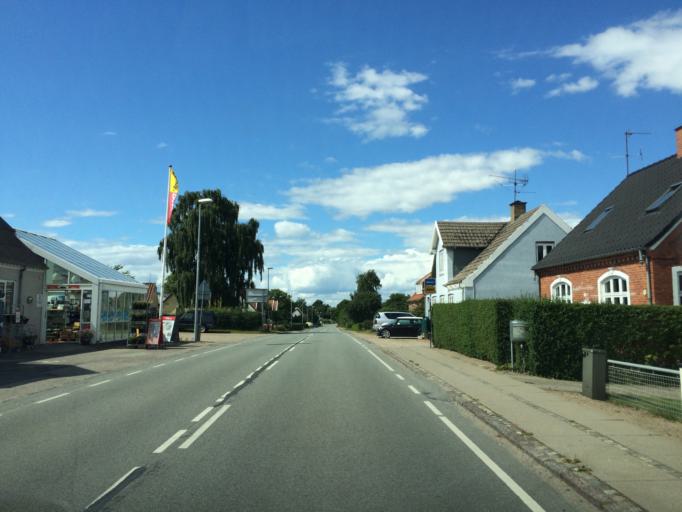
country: DK
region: South Denmark
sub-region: Faaborg-Midtfyn Kommune
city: Faaborg
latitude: 55.1308
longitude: 10.2110
